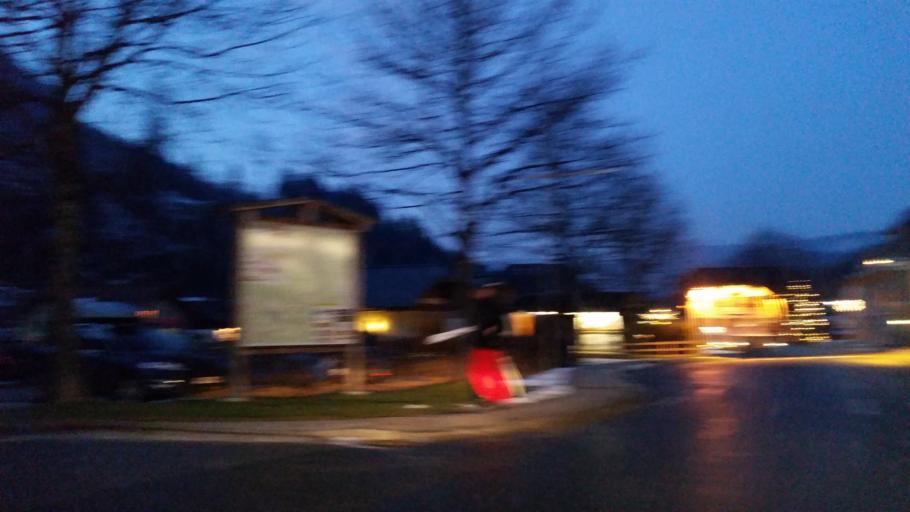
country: AT
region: Salzburg
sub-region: Politischer Bezirk Hallein
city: Abtenau
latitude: 47.5126
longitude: 13.4313
